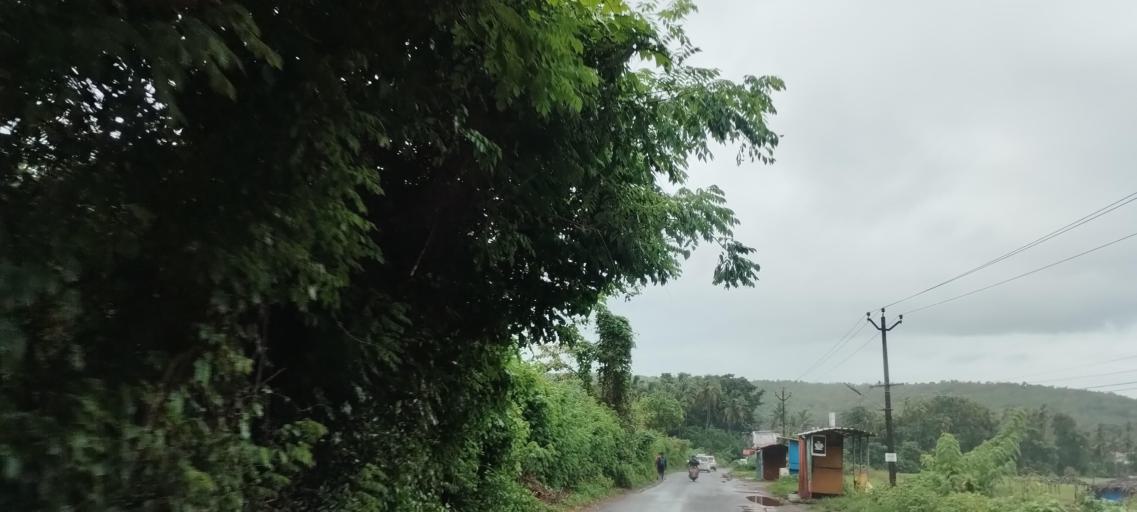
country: IN
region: Goa
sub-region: North Goa
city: Solim
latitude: 15.5930
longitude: 73.7719
